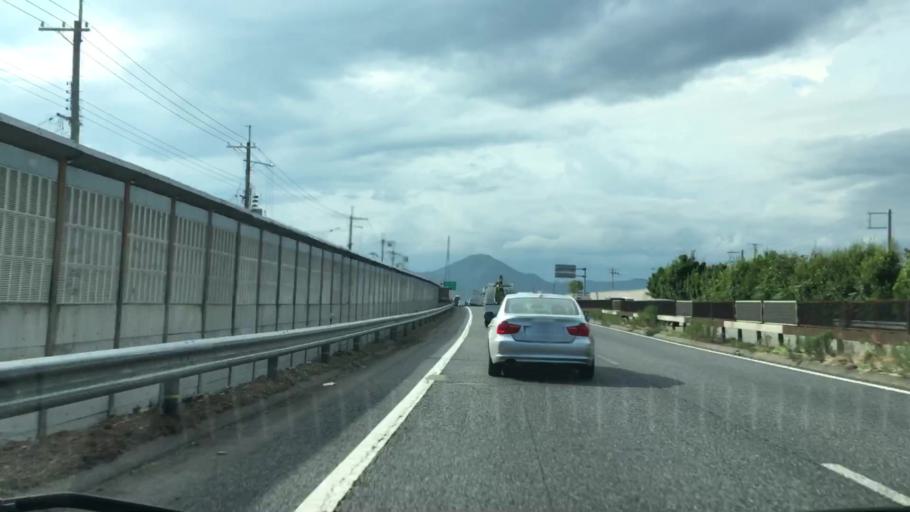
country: JP
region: Hyogo
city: Kakogawacho-honmachi
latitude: 34.7808
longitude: 134.8335
